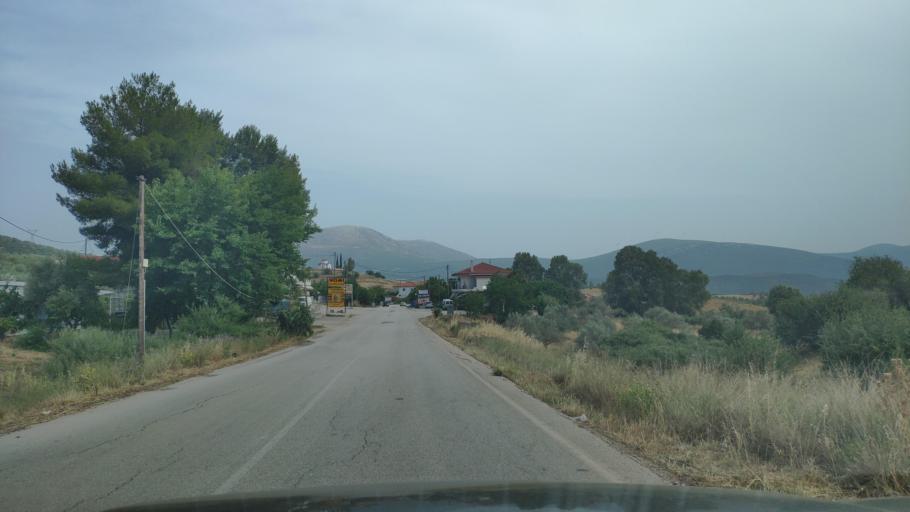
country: GR
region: Peloponnese
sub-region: Nomos Argolidos
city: Palaia Epidavros
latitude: 37.5630
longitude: 23.1518
